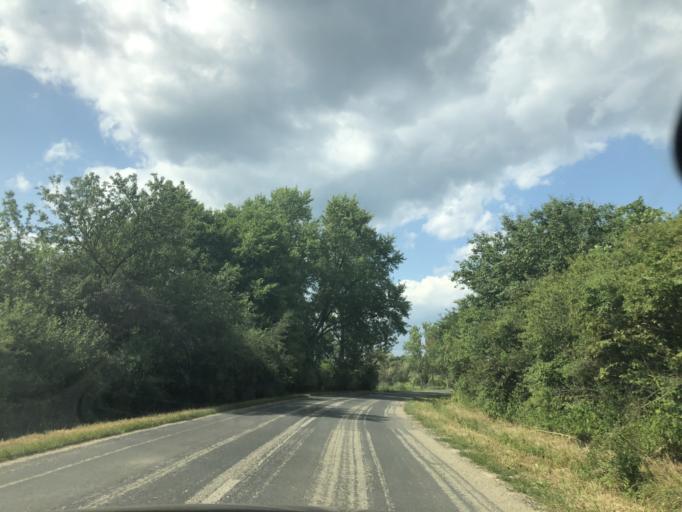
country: HU
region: Borsod-Abauj-Zemplen
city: Szendro
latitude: 48.4506
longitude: 20.7968
